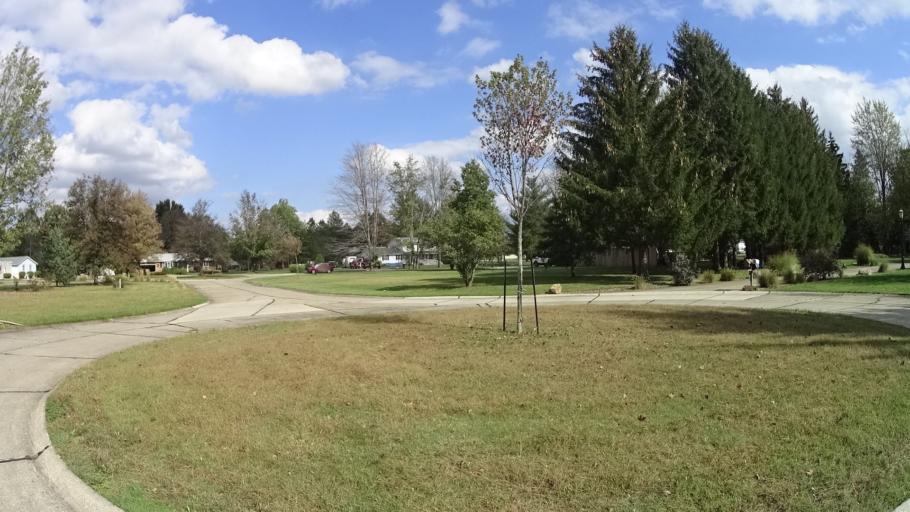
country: US
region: Ohio
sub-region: Lorain County
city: Grafton
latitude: 41.2620
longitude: -82.0600
